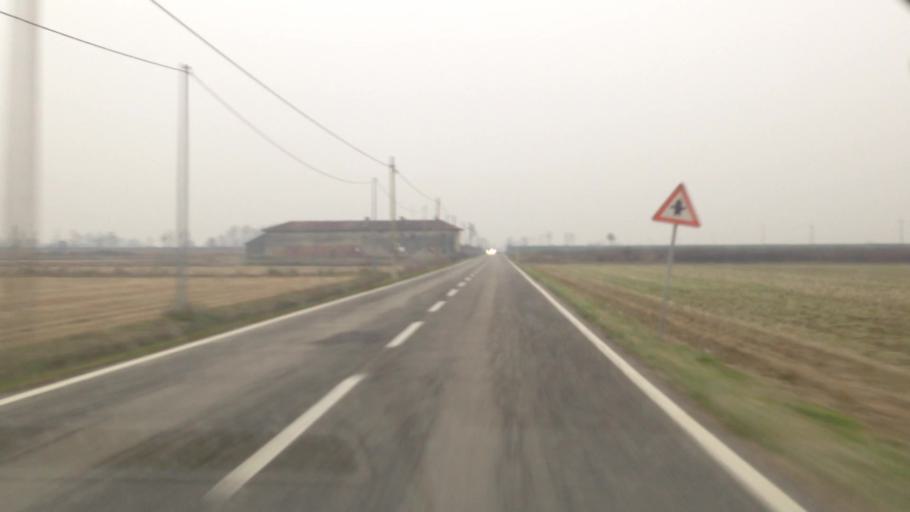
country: IT
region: Piedmont
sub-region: Provincia di Vercelli
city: Lamporo
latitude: 45.2240
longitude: 8.1007
